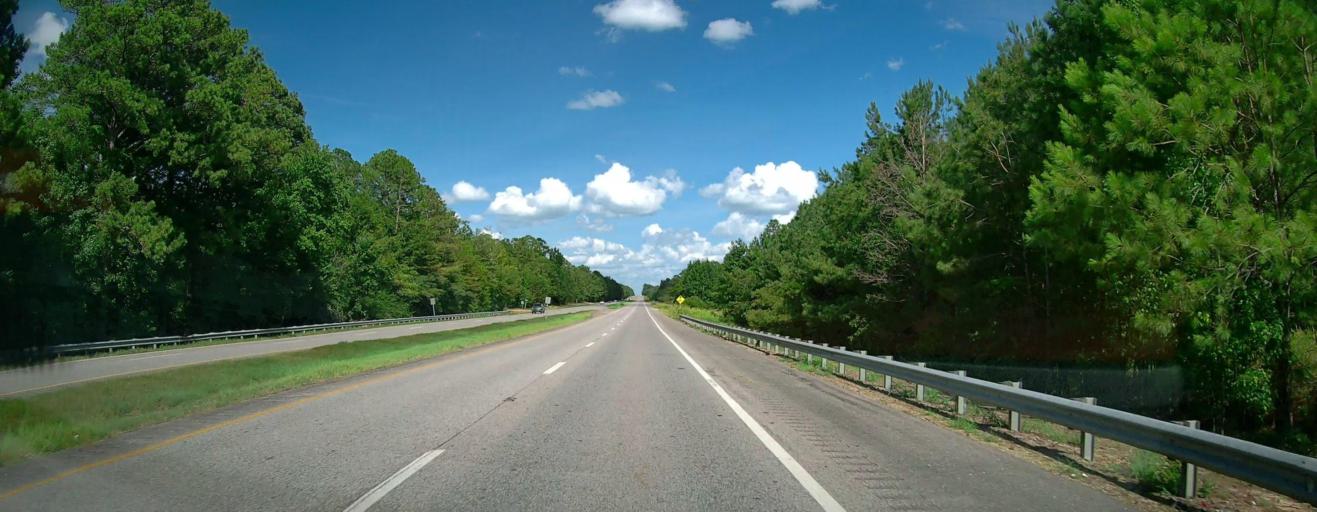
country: US
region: Alabama
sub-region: Pickens County
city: Gordo
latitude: 33.2838
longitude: -87.8328
